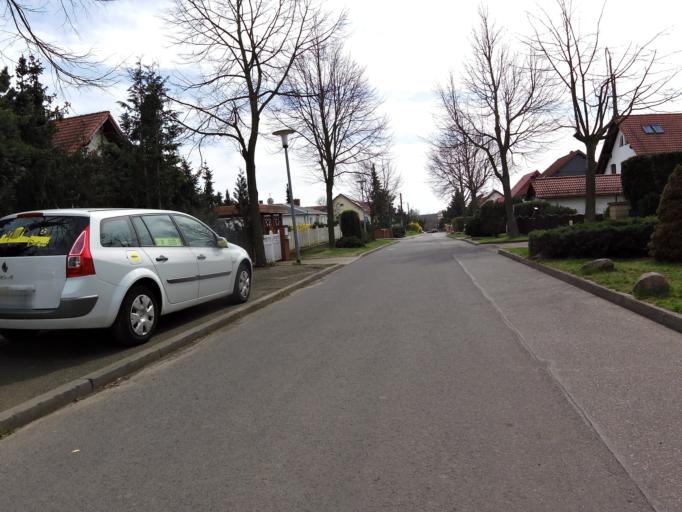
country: DE
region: Saxony
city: Schkeuditz
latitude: 51.3886
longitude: 12.2744
